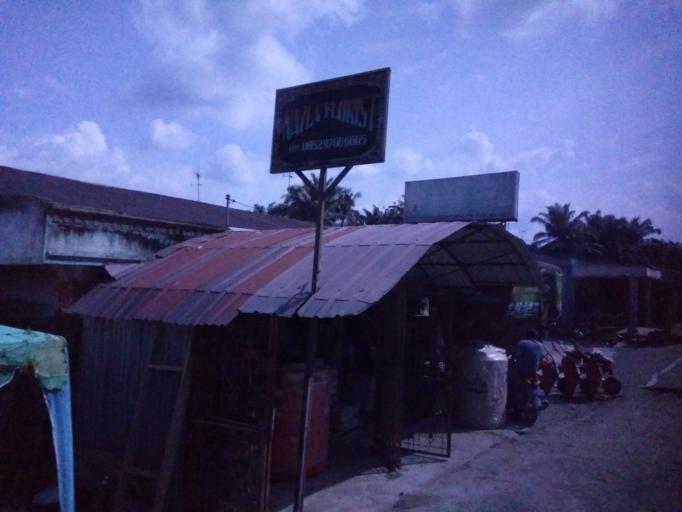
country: ID
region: North Sumatra
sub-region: Kabupaten Langkat
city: Stabat
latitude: 3.6979
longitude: 98.1561
